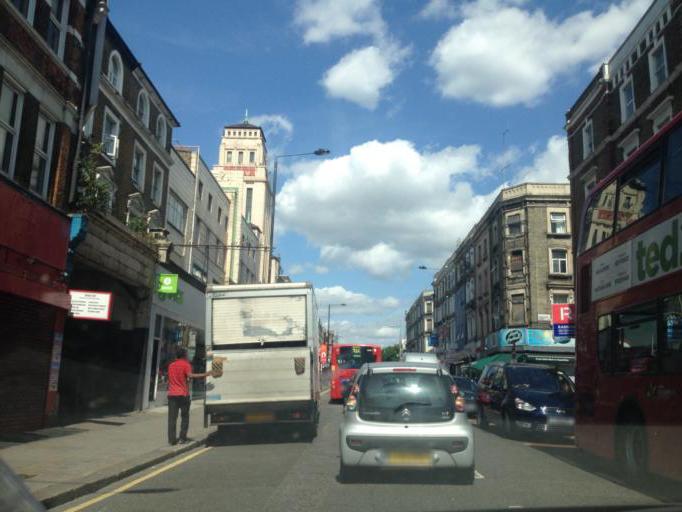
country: GB
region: England
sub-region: Greater London
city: Belsize Park
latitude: 51.5410
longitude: -0.1970
